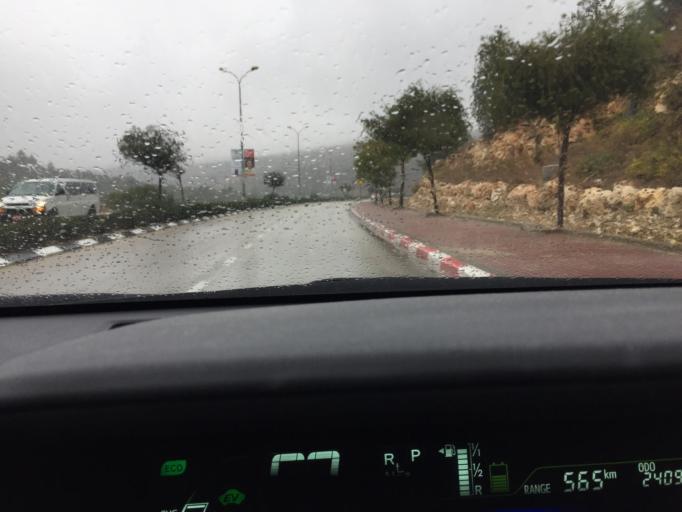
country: IL
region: Jerusalem
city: Ariel
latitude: 32.1006
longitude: 35.1662
